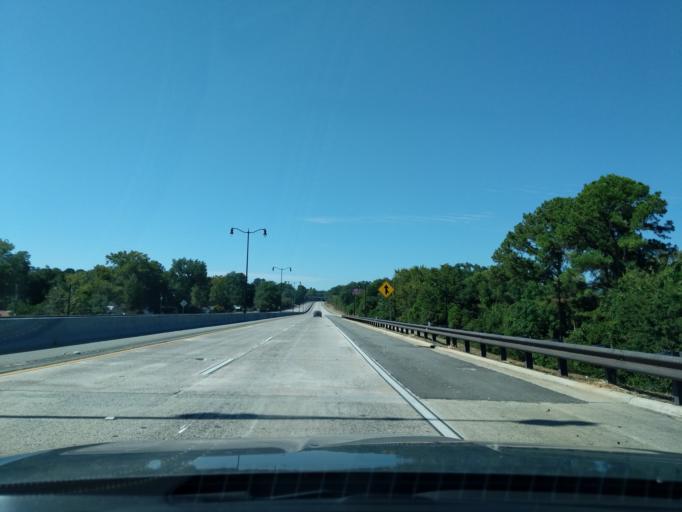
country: US
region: Georgia
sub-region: Richmond County
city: Augusta
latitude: 33.4838
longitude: -81.9971
